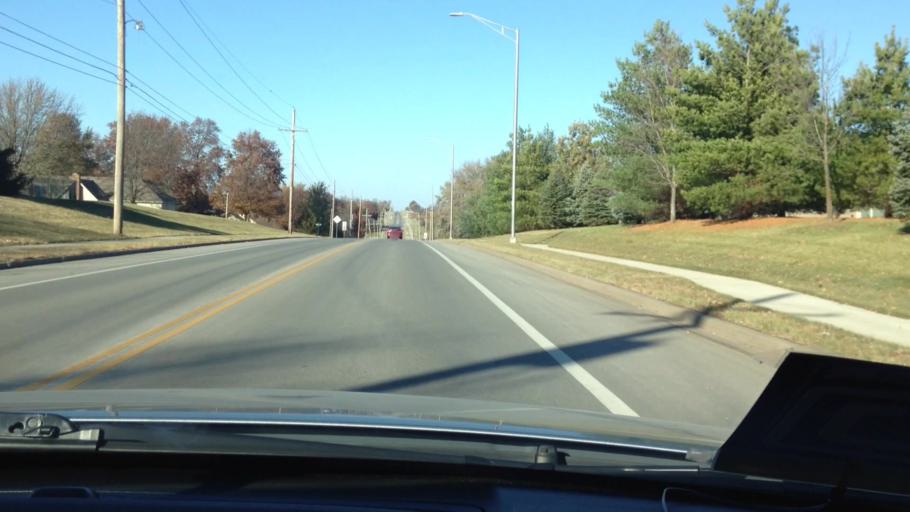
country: US
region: Kansas
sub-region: Johnson County
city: Olathe
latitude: 38.9086
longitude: -94.8160
